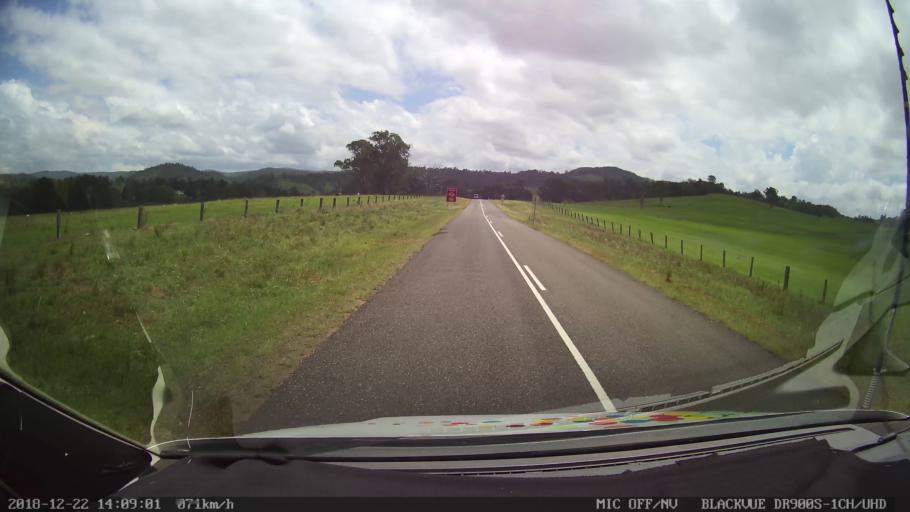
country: AU
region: New South Wales
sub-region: Clarence Valley
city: Coutts Crossing
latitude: -29.9835
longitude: 152.7214
